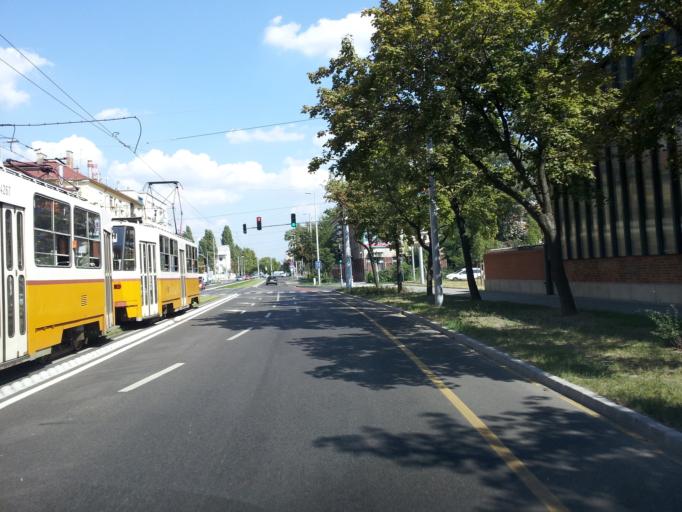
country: HU
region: Budapest
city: Budapest XI. keruelet
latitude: 47.4620
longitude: 19.0450
